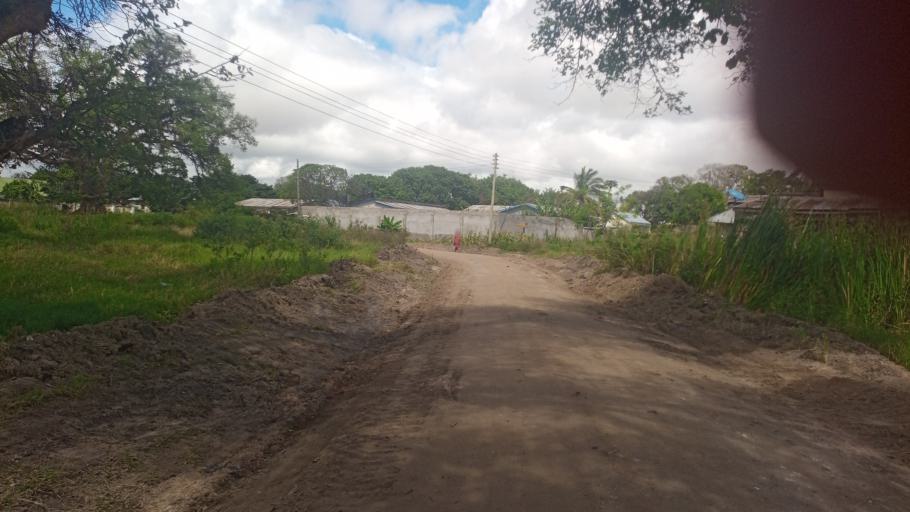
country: TZ
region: Dodoma
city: Dodoma
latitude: -6.1915
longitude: 35.7295
